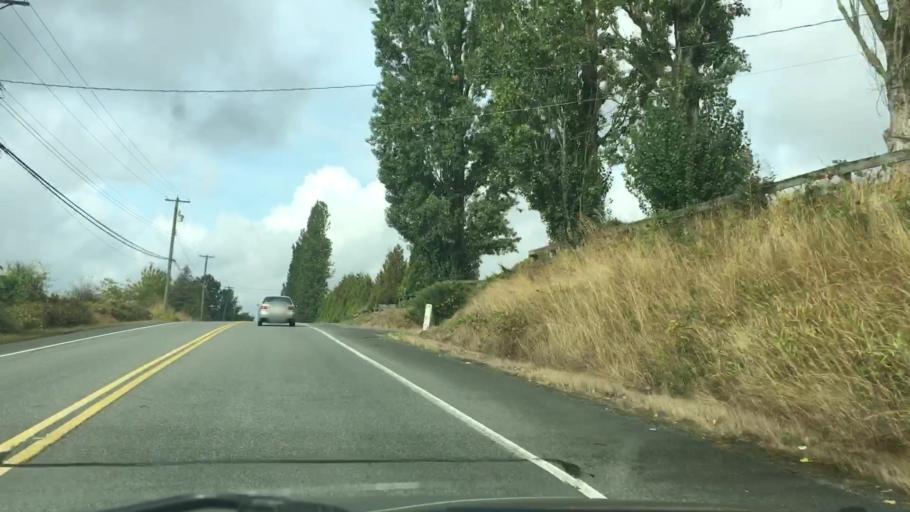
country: CA
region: British Columbia
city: Langley
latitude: 49.1044
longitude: -122.5936
